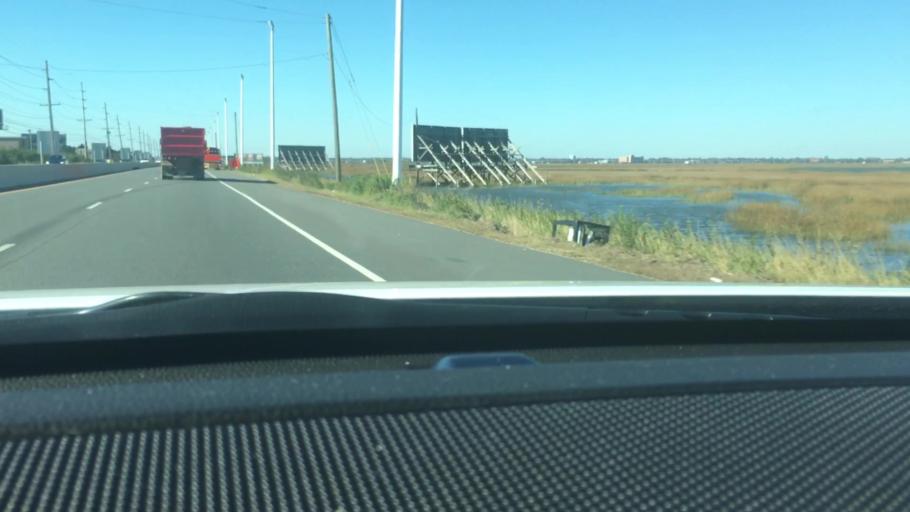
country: US
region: New Jersey
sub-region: Atlantic County
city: Ventnor City
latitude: 39.3865
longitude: -74.4664
